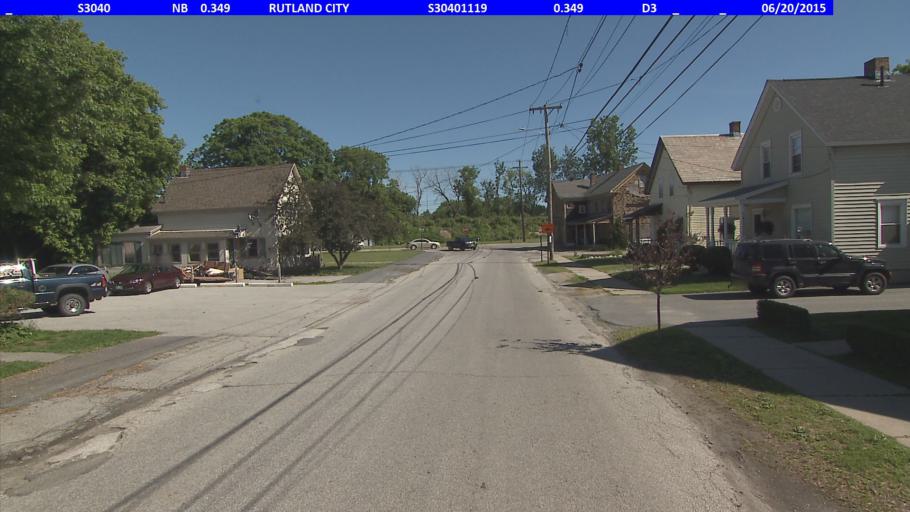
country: US
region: Vermont
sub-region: Rutland County
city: Rutland
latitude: 43.6062
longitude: -72.9868
